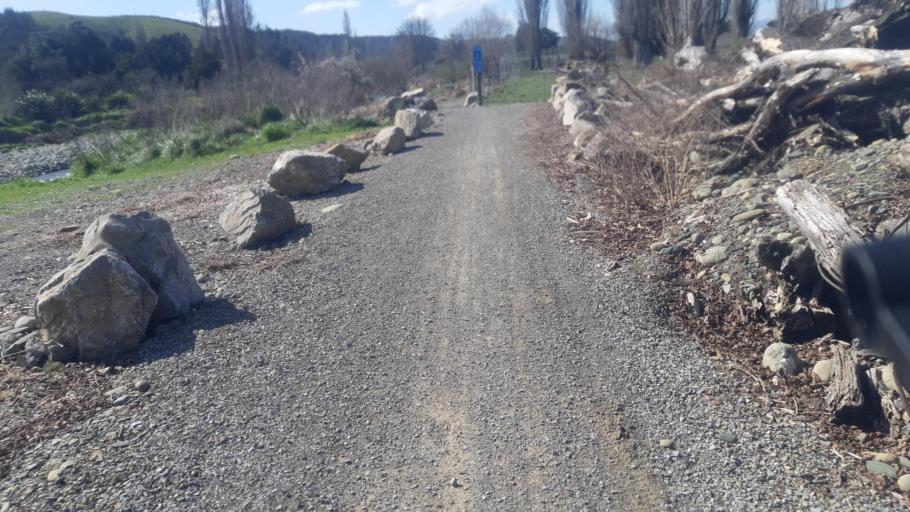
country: NZ
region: Tasman
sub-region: Tasman District
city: Wakefield
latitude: -41.4162
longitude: 173.0040
